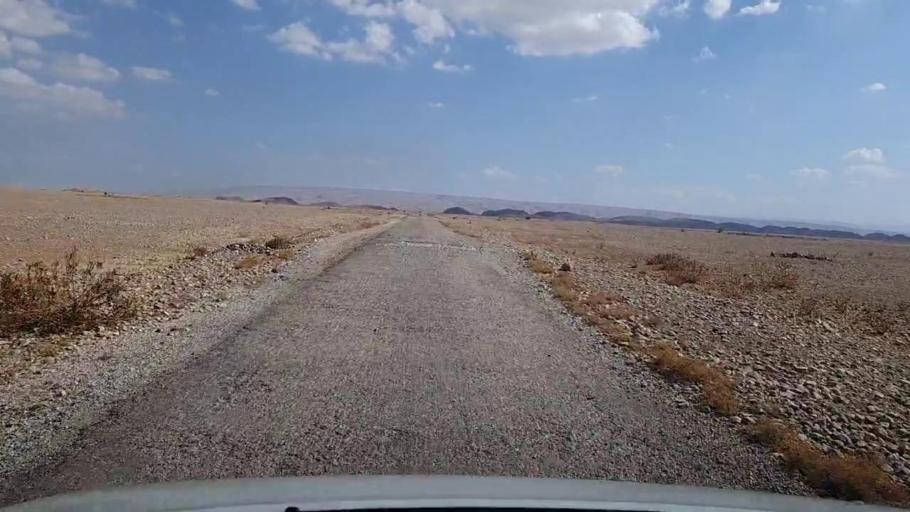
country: PK
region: Sindh
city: Bhan
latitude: 26.3695
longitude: 67.6409
